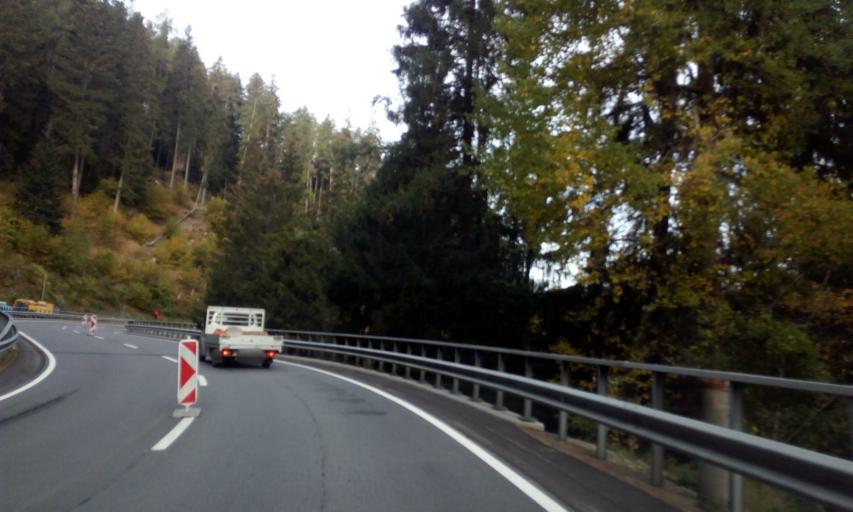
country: CH
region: Grisons
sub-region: Hinterrhein District
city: Thusis
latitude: 46.6937
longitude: 9.4810
